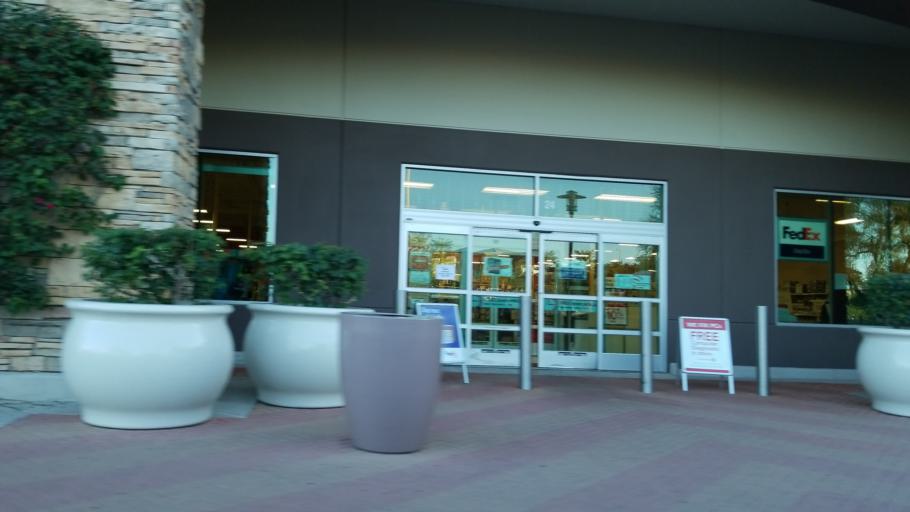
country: US
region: Arizona
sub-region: Maricopa County
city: Paradise Valley
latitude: 33.6745
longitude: -111.9729
